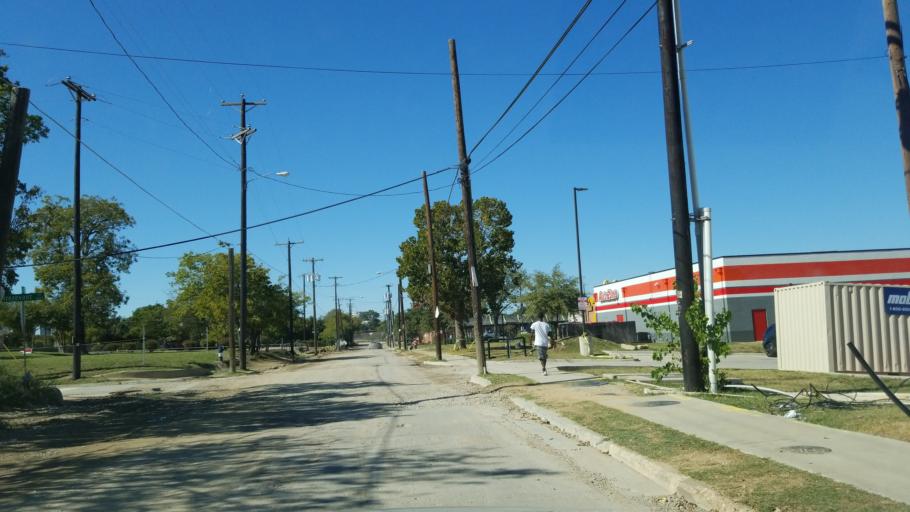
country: US
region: Texas
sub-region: Dallas County
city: Dallas
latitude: 32.7752
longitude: -96.7640
